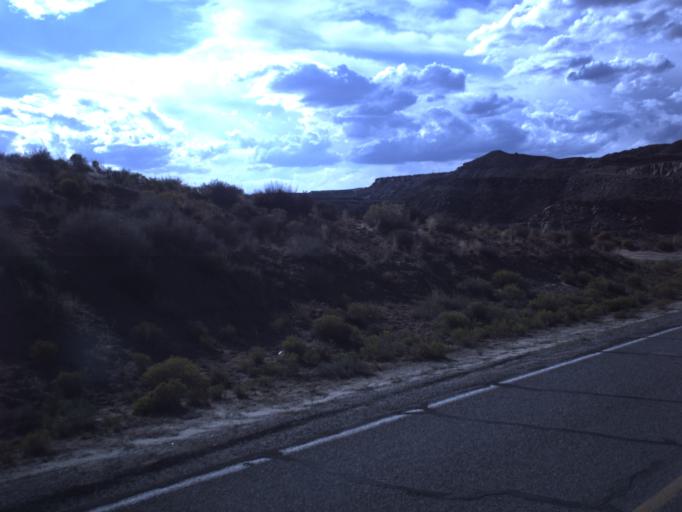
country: US
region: Utah
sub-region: San Juan County
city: Blanding
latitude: 37.3191
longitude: -109.3097
